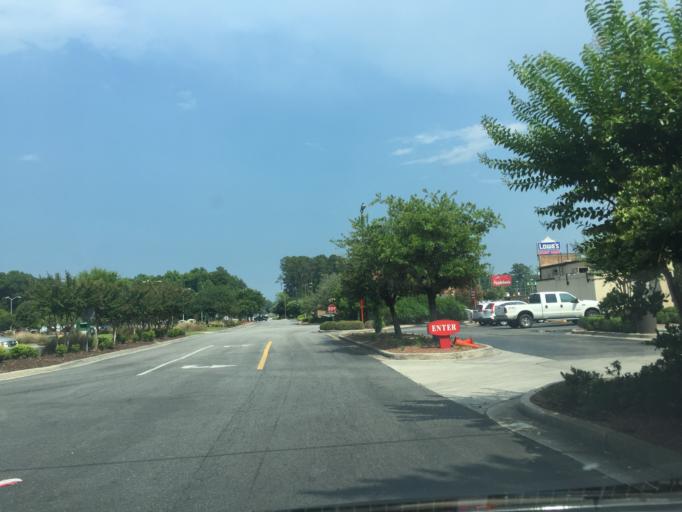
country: US
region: Georgia
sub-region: Chatham County
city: Montgomery
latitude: 31.9811
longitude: -81.1441
